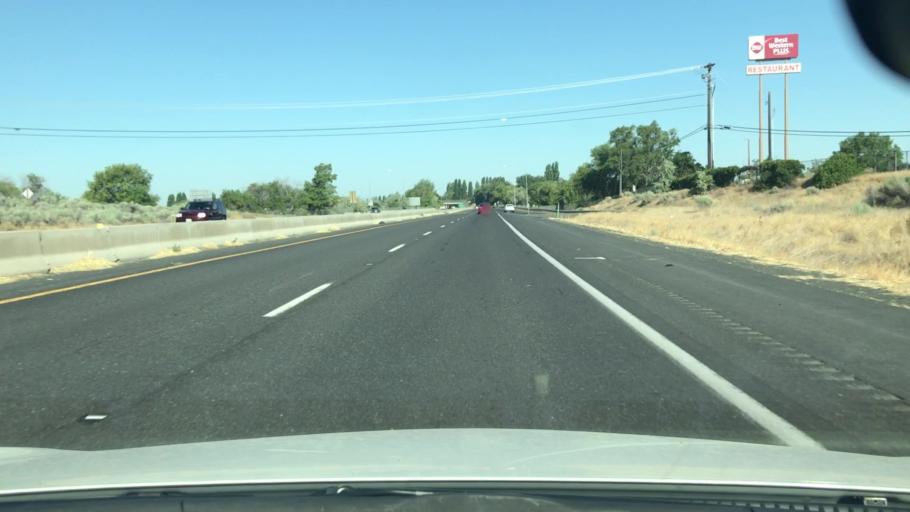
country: US
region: Washington
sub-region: Grant County
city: Cascade Valley
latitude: 47.1015
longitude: -119.3177
